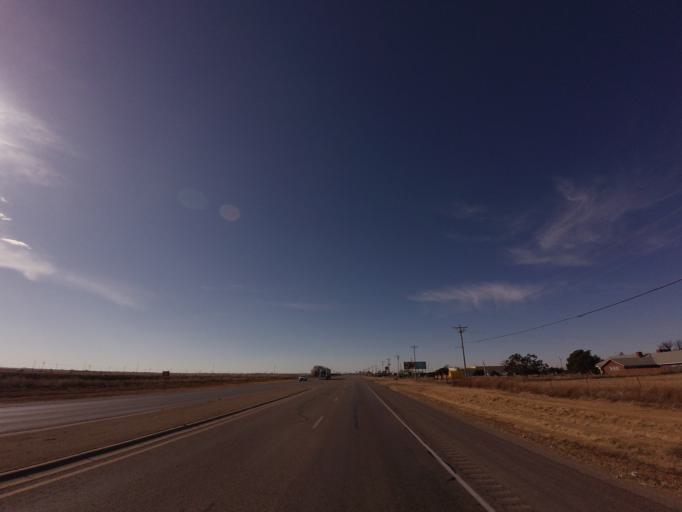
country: US
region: New Mexico
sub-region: Curry County
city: Texico
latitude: 34.3931
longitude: -103.1279
